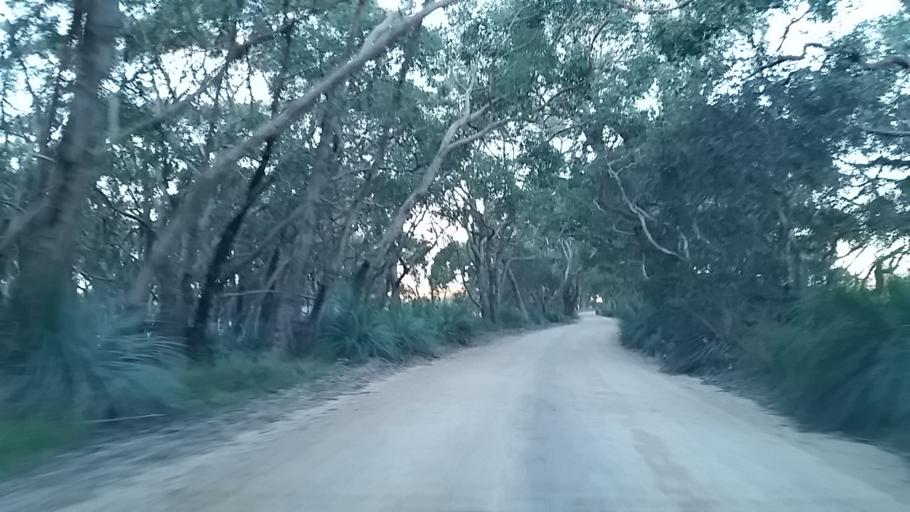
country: AU
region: South Australia
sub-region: Alexandrina
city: Mount Compass
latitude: -35.2807
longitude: 138.5951
